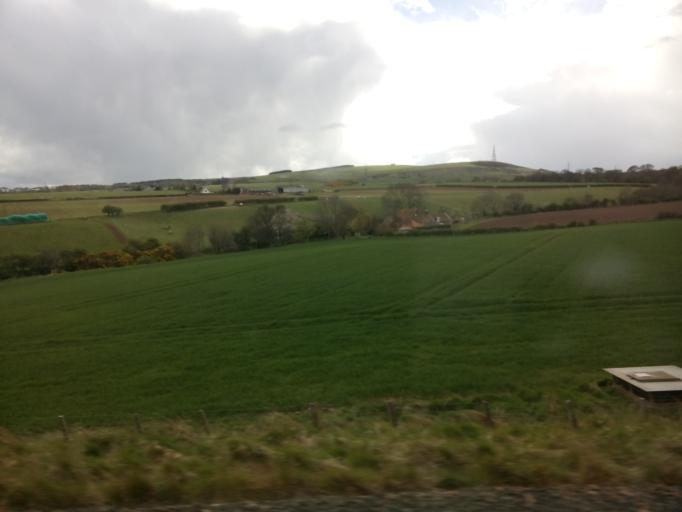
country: GB
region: Scotland
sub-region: East Lothian
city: Dunbar
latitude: 55.9607
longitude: -2.4137
